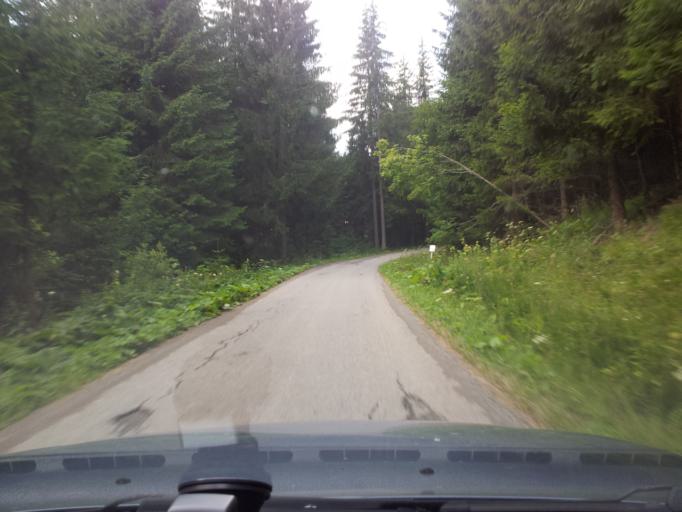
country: SK
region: Zilinsky
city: Oravska Lesna
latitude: 49.3860
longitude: 19.1823
